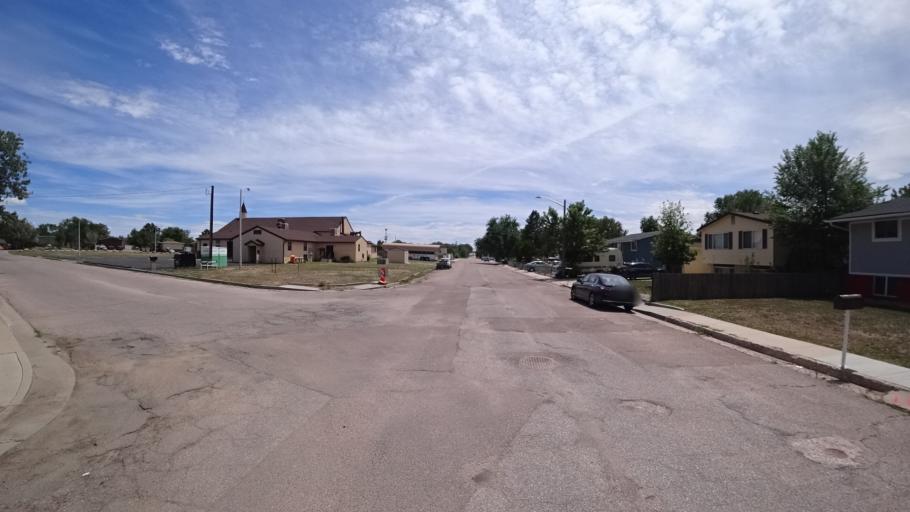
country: US
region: Colorado
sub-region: El Paso County
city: Security-Widefield
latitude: 38.7288
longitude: -104.7283
